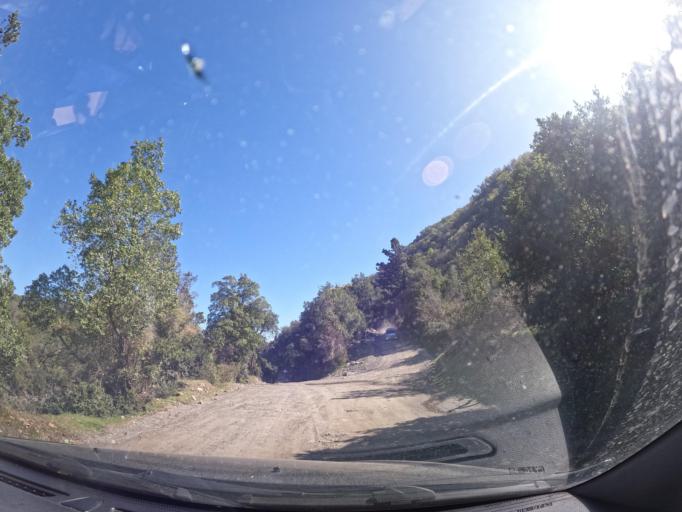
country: CL
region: Maule
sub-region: Provincia de Linares
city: Longavi
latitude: -36.2295
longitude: -71.4000
